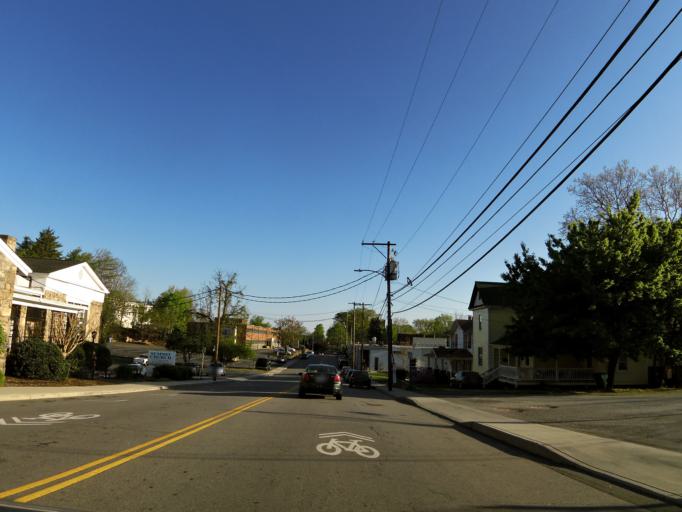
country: US
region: North Carolina
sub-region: Buncombe County
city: Asheville
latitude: 35.5933
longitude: -82.5588
